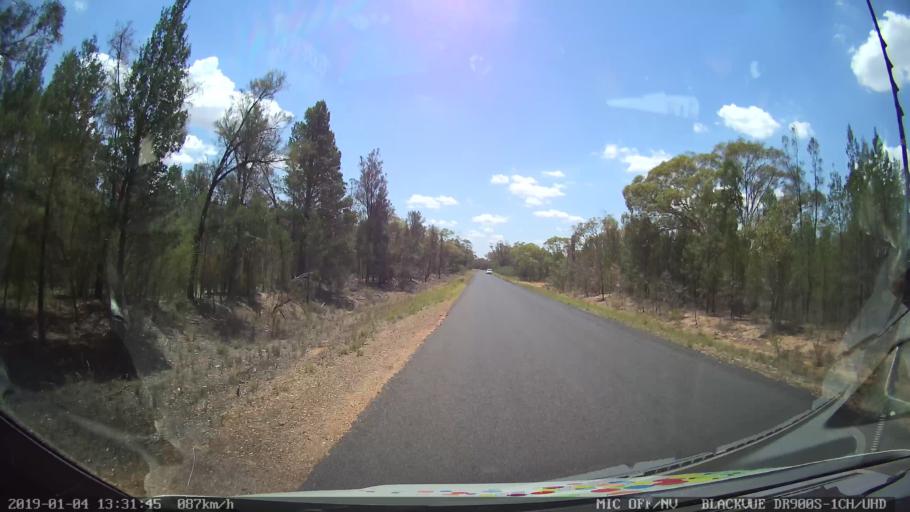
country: AU
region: New South Wales
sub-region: Parkes
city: Peak Hill
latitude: -32.6186
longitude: 148.5488
